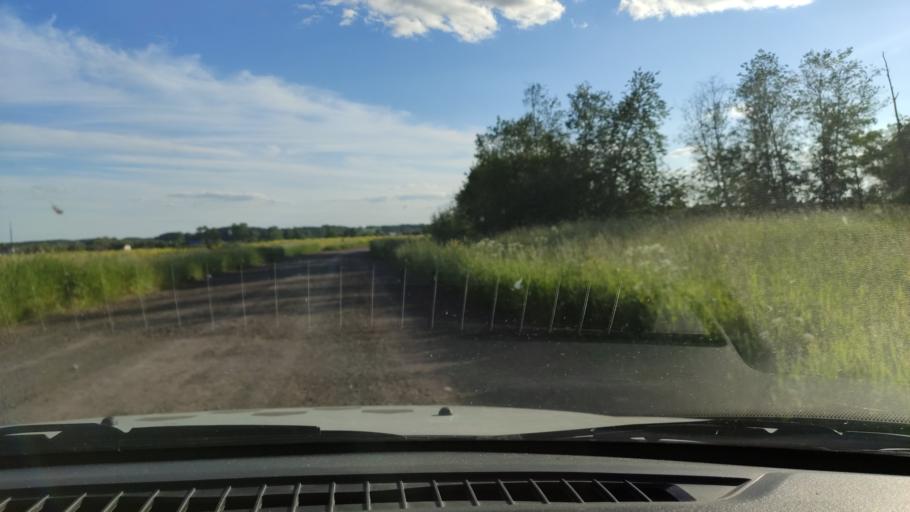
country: RU
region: Perm
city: Orda
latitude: 57.3004
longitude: 56.6264
